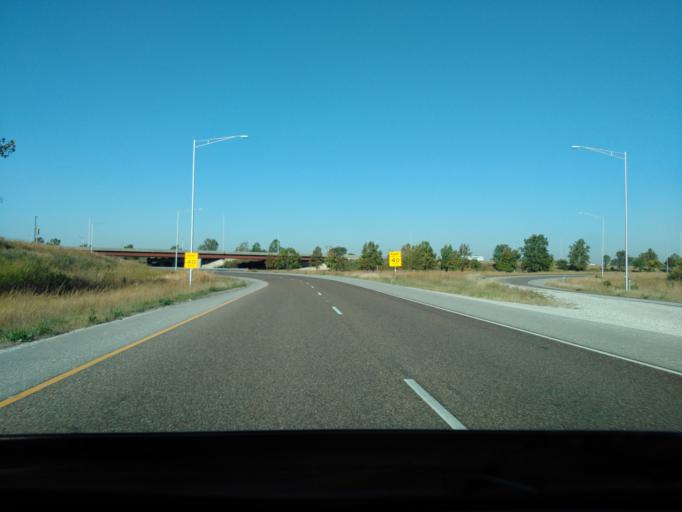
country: US
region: Illinois
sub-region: Saint Clair County
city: Caseyville
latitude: 38.6758
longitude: -90.0268
